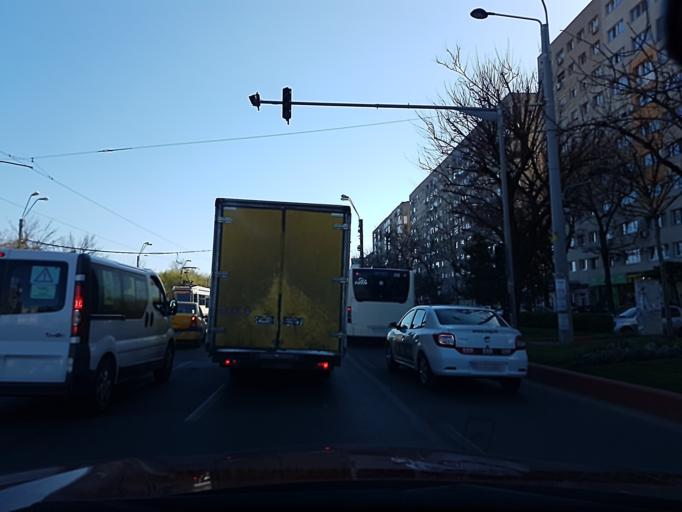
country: RO
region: Bucuresti
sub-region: Municipiul Bucuresti
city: Bucharest
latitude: 44.4288
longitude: 26.1388
